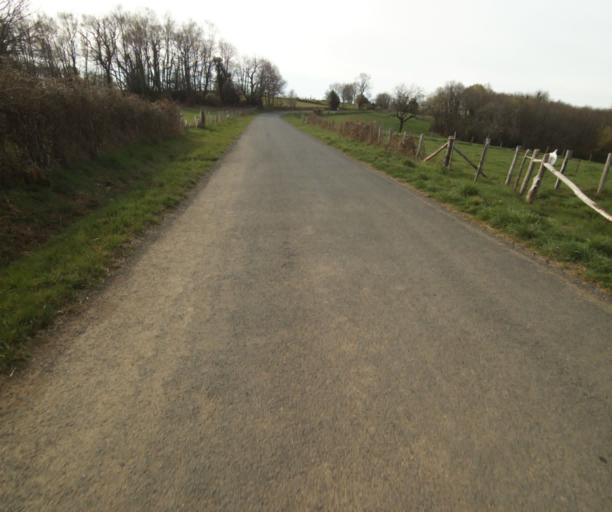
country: FR
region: Limousin
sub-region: Departement de la Correze
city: Chamboulive
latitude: 45.4169
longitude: 1.7833
